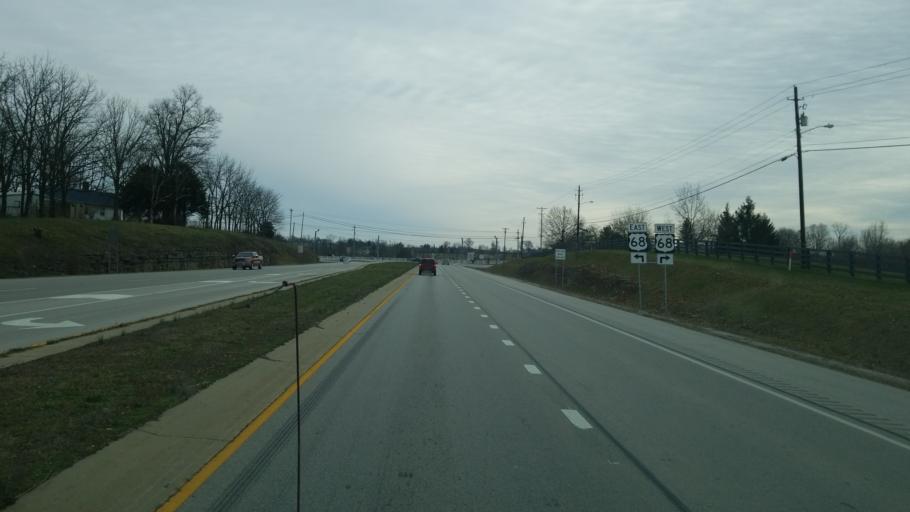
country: US
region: Kentucky
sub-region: Bourbon County
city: Paris
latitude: 38.2226
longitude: -84.2379
